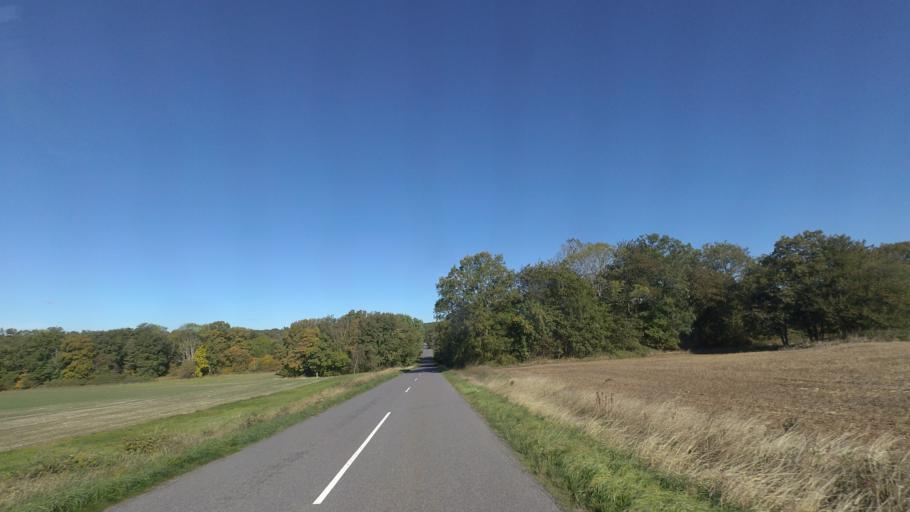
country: DK
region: Capital Region
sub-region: Bornholm Kommune
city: Nexo
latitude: 55.0751
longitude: 15.0806
